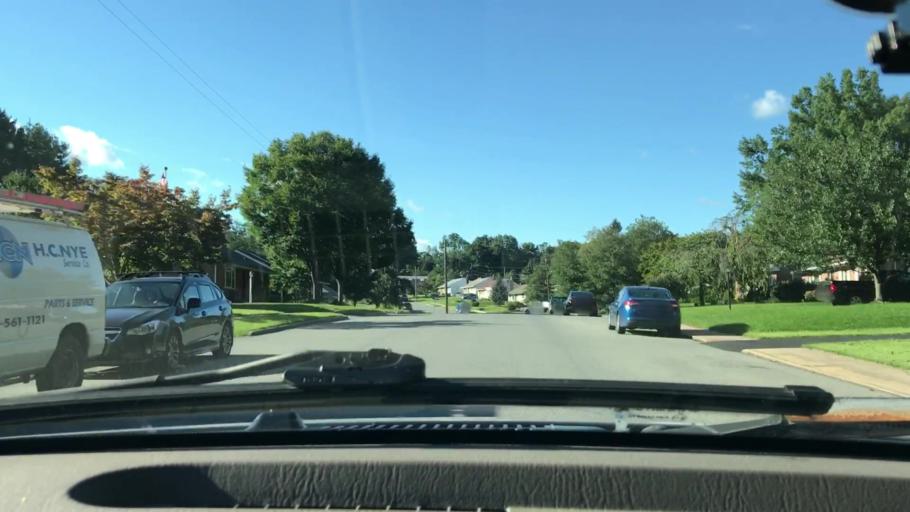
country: US
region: Pennsylvania
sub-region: Lancaster County
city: Elizabethtown
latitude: 40.1601
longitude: -76.6051
